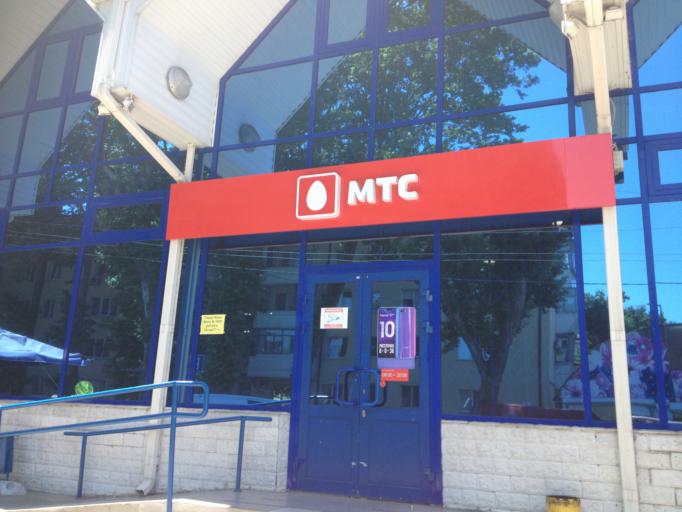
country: RU
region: Krasnodarskiy
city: Anapa
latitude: 44.8996
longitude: 37.3258
